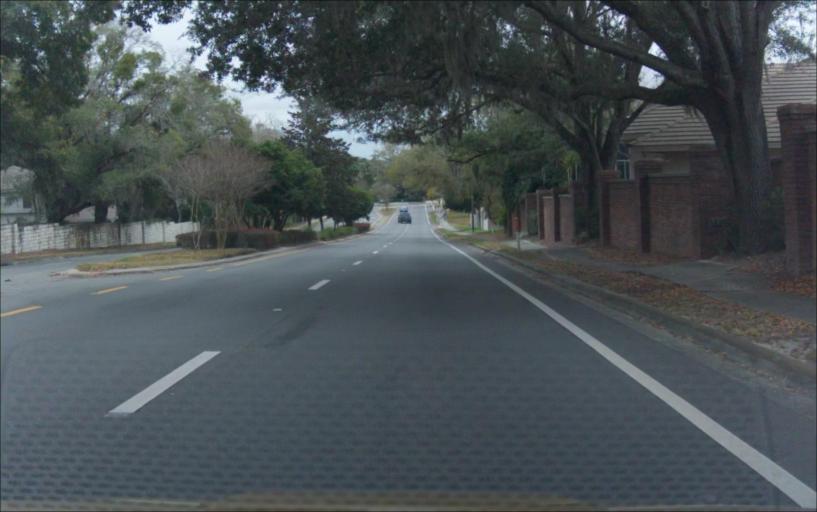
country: US
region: Florida
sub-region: Orange County
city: Winter Park
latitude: 28.6250
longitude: -81.3271
